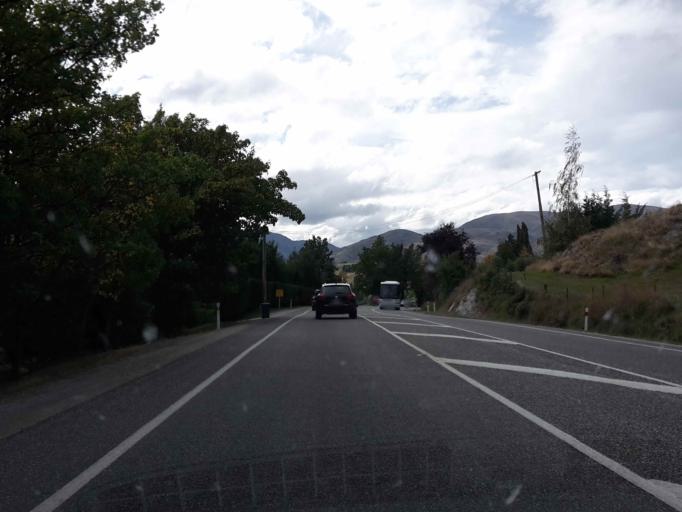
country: NZ
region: Otago
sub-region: Queenstown-Lakes District
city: Arrowtown
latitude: -44.9928
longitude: 168.8067
